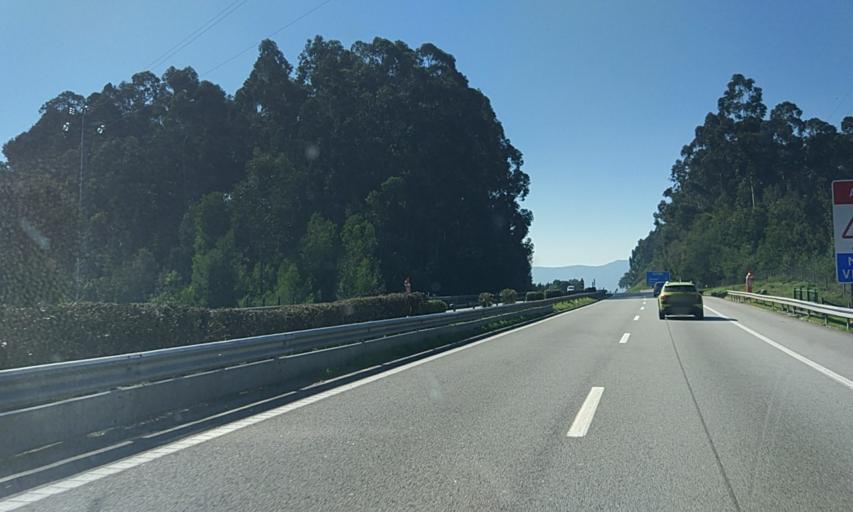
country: PT
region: Porto
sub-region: Paredes
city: Recarei
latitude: 41.1679
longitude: -8.3915
